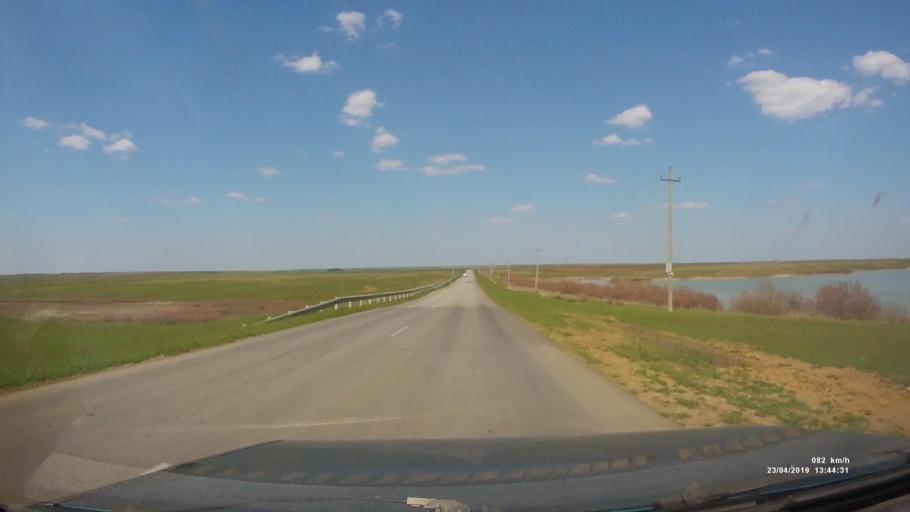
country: RU
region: Kalmykiya
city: Yashalta
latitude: 46.5812
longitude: 42.8167
